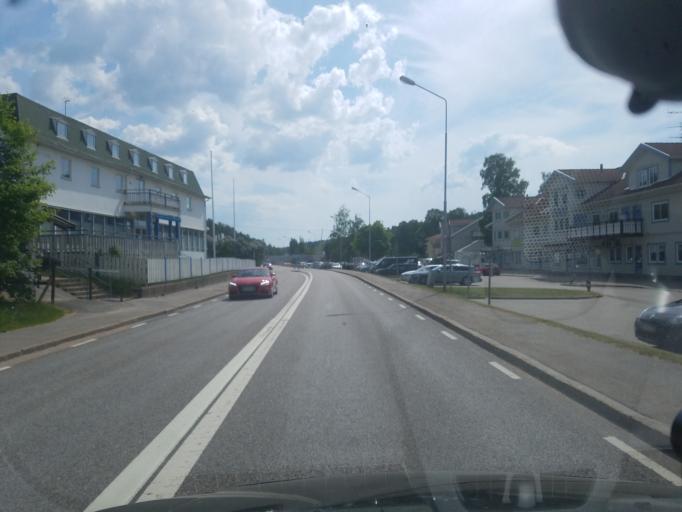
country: SE
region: Vaestra Goetaland
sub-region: Orust
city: Henan
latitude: 58.2382
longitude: 11.6803
